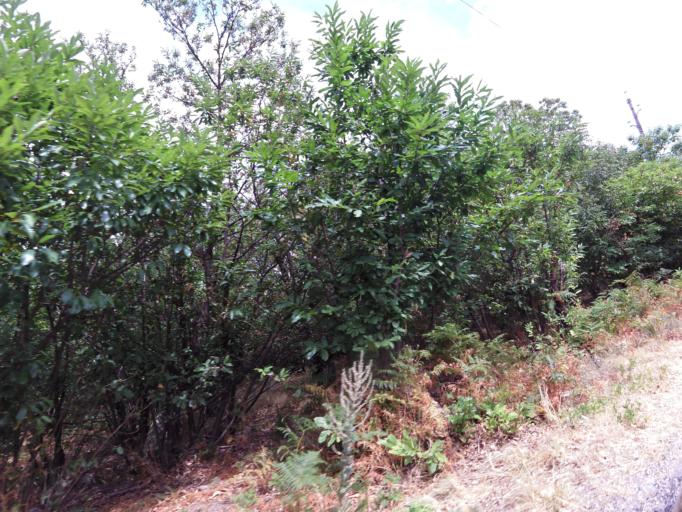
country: FR
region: Languedoc-Roussillon
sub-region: Departement du Gard
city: Le Vigan
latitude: 44.0263
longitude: 3.6239
